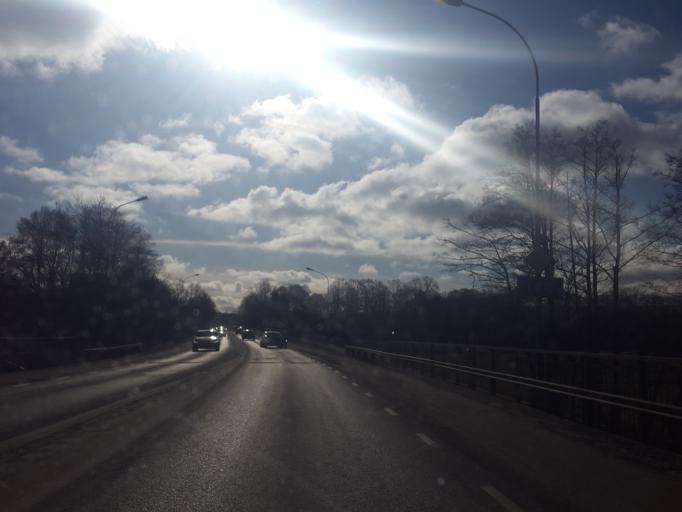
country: SE
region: Vaestra Goetaland
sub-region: Alingsas Kommun
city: Alingsas
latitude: 57.9338
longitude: 12.5444
